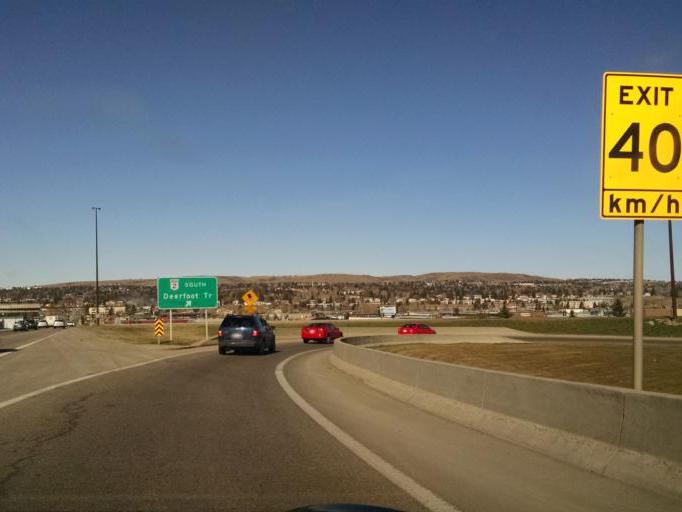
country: CA
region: Alberta
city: Calgary
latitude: 51.0963
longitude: -114.0425
